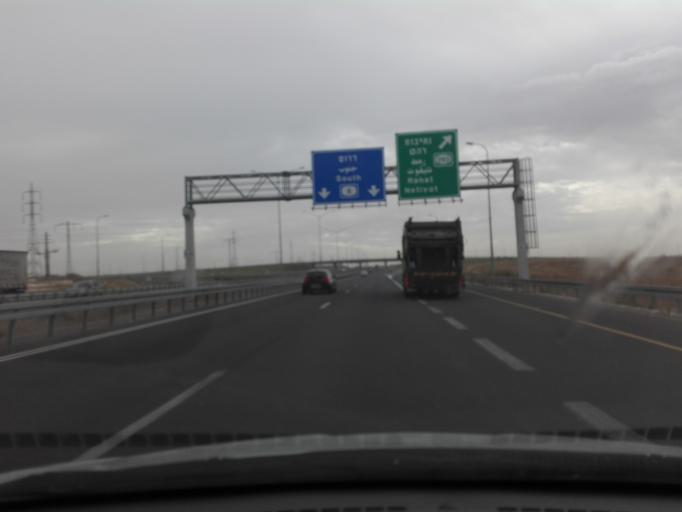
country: IL
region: Southern District
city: Lehavim
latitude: 31.4467
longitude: 34.7710
